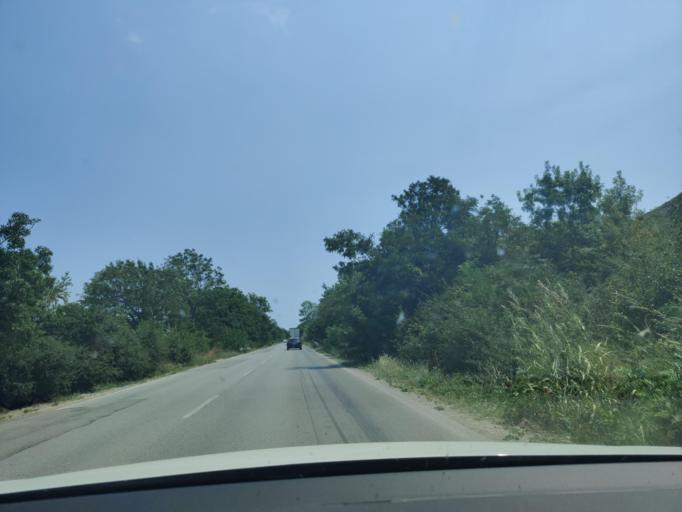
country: BG
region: Montana
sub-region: Obshtina Montana
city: Montana
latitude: 43.4399
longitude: 23.1148
